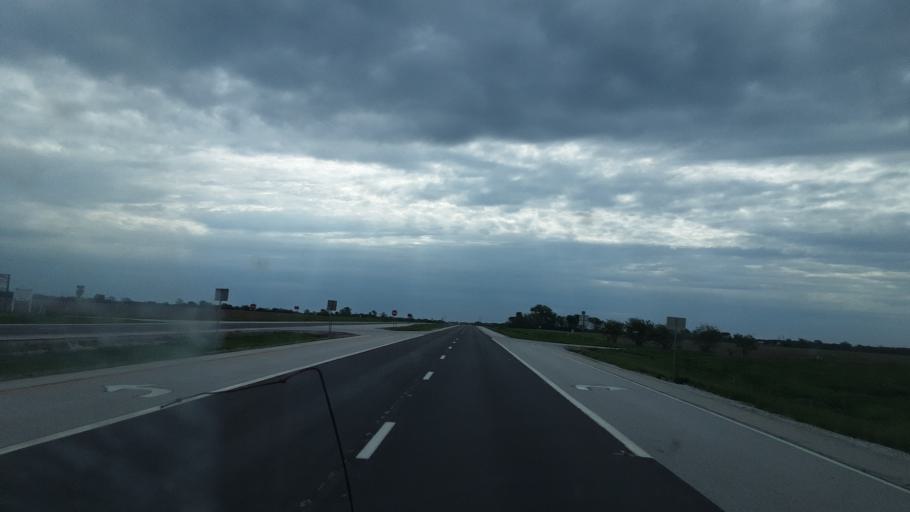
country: US
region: Illinois
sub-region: McDonough County
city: Colchester
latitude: 40.4065
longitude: -90.8411
